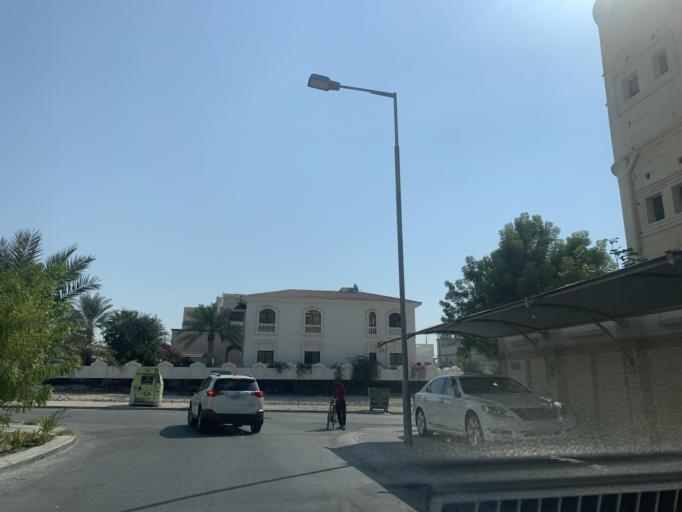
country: BH
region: Central Governorate
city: Madinat Hamad
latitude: 26.1107
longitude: 50.4976
